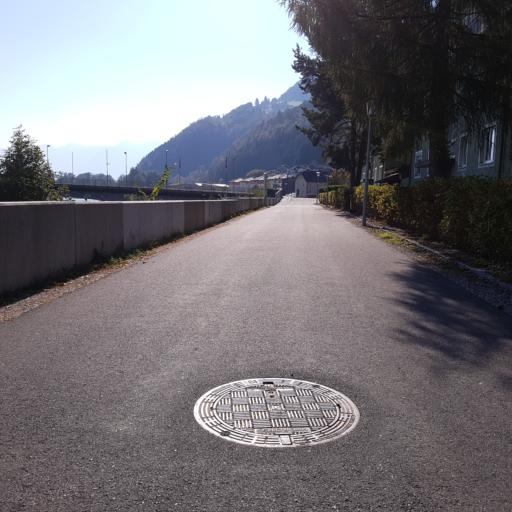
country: AT
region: Salzburg
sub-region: Politischer Bezirk Hallein
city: Hallein
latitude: 47.6778
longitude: 13.0984
